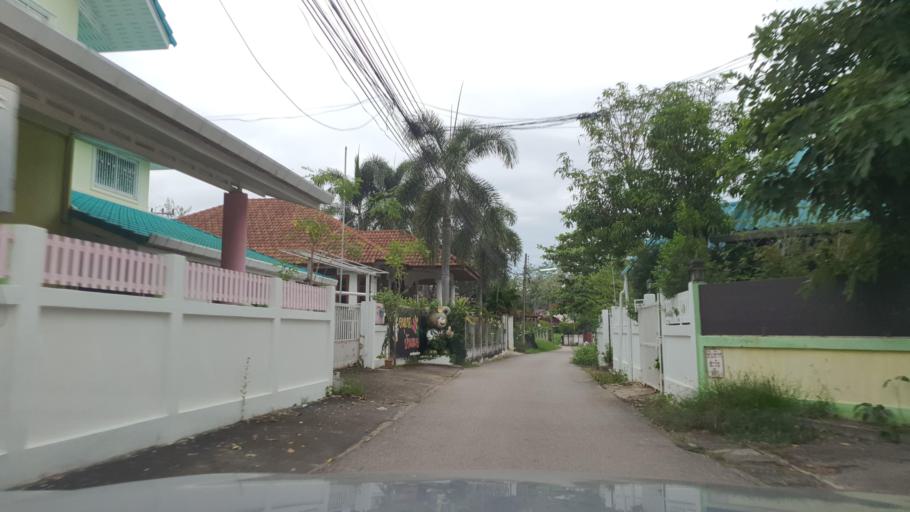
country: TH
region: Chiang Mai
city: San Sai
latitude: 18.9180
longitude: 98.9450
